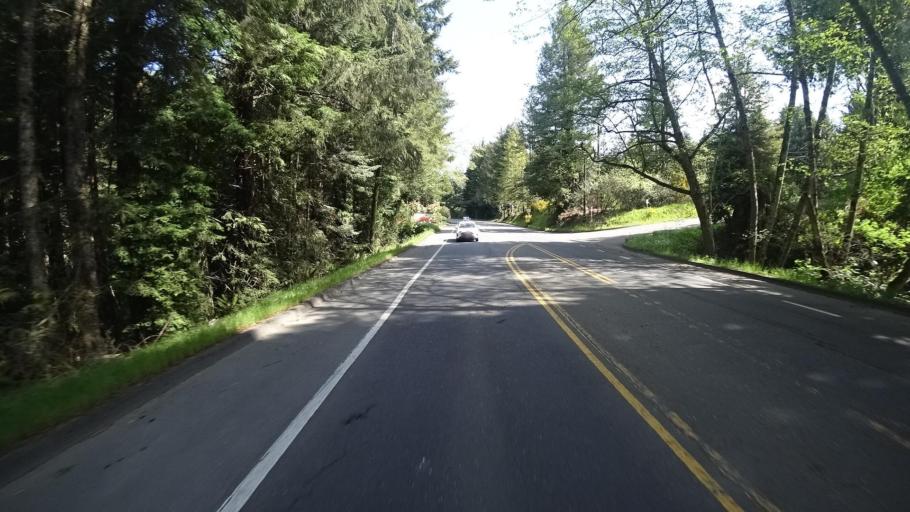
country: US
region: California
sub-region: Humboldt County
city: Pine Hills
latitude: 40.7498
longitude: -124.1463
